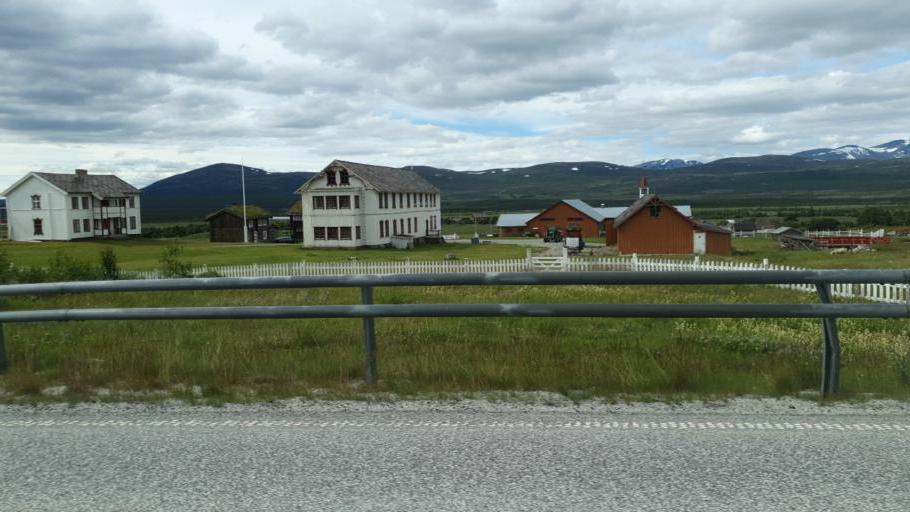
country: NO
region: Oppland
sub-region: Dovre
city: Dovre
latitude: 62.1134
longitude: 9.2886
